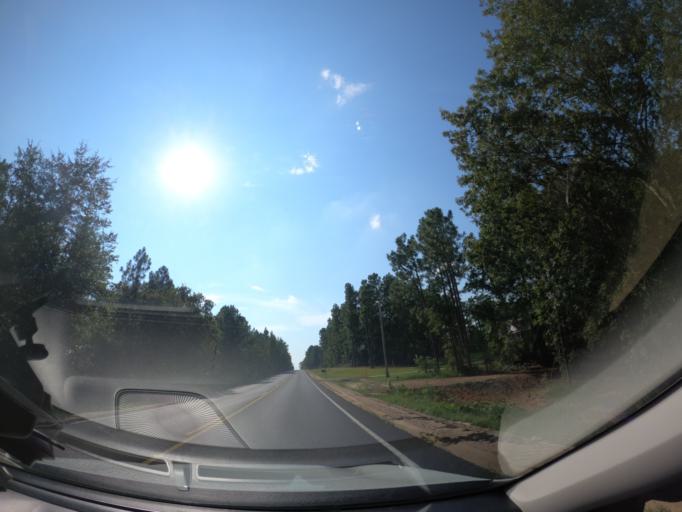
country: US
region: South Carolina
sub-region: Aiken County
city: Jackson
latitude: 33.4024
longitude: -81.7685
